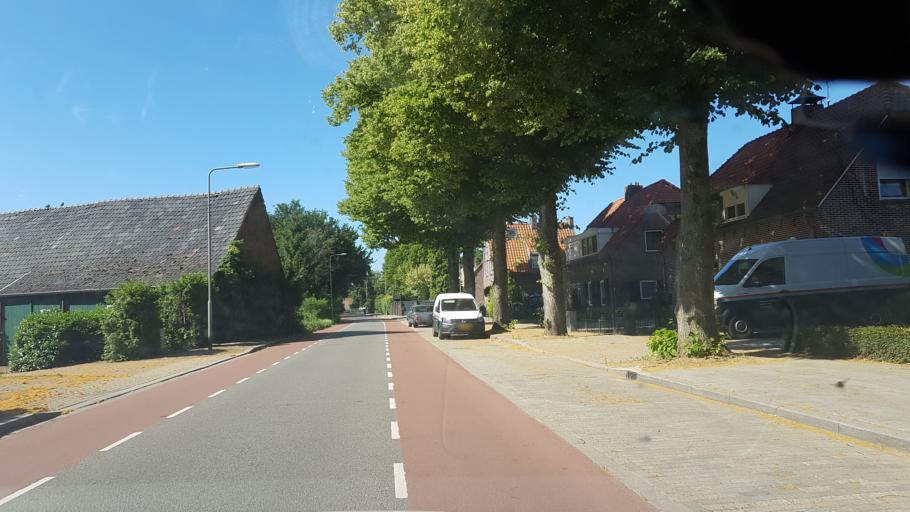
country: NL
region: Limburg
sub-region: Gemeente Gennep
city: Gennep
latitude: 51.7246
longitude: 5.9525
